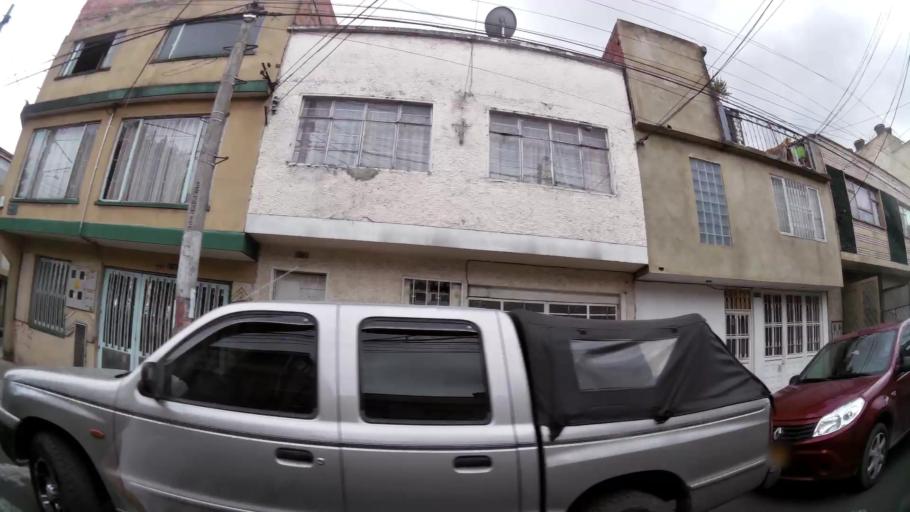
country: CO
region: Bogota D.C.
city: Bogota
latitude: 4.6759
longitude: -74.0901
